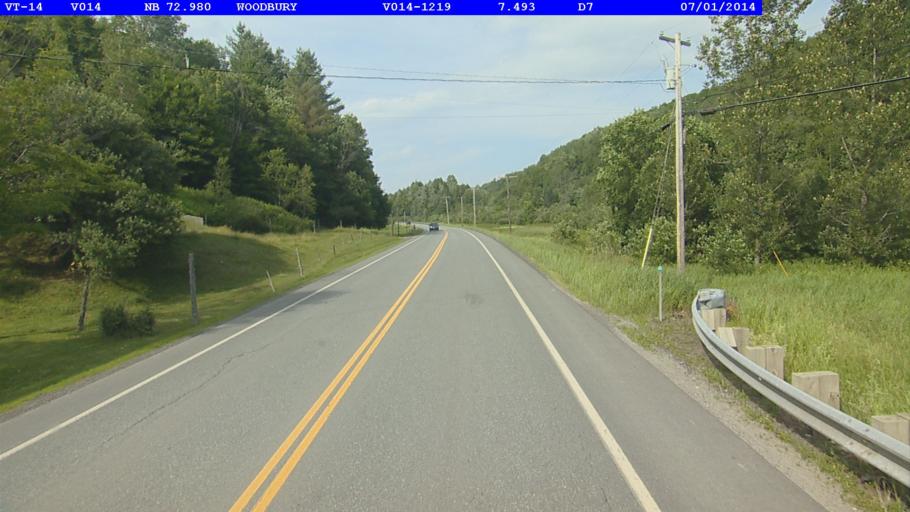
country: US
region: Vermont
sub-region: Caledonia County
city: Hardwick
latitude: 44.4836
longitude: -72.3838
